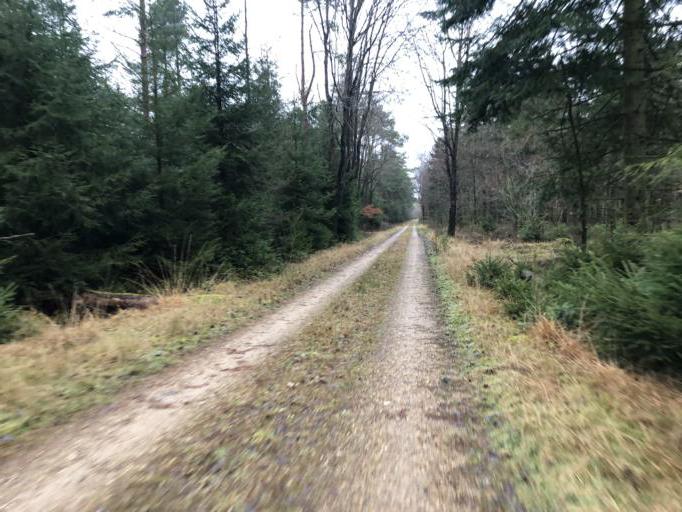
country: DK
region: Central Jutland
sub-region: Holstebro Kommune
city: Ulfborg
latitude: 56.2916
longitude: 8.4348
